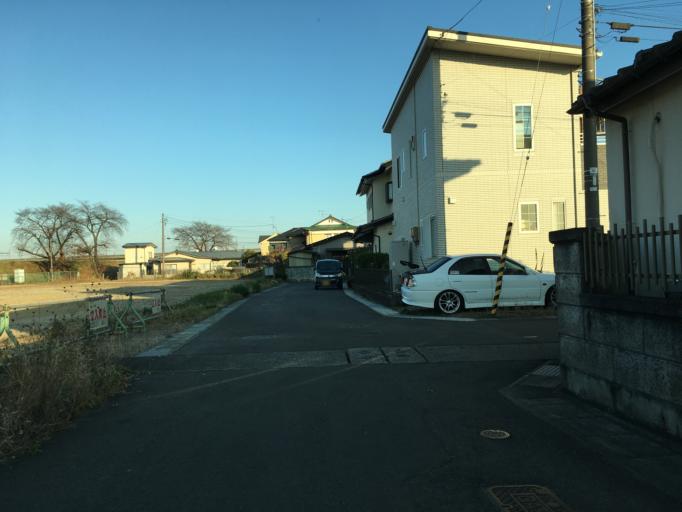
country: JP
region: Fukushima
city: Fukushima-shi
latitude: 37.8118
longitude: 140.4807
